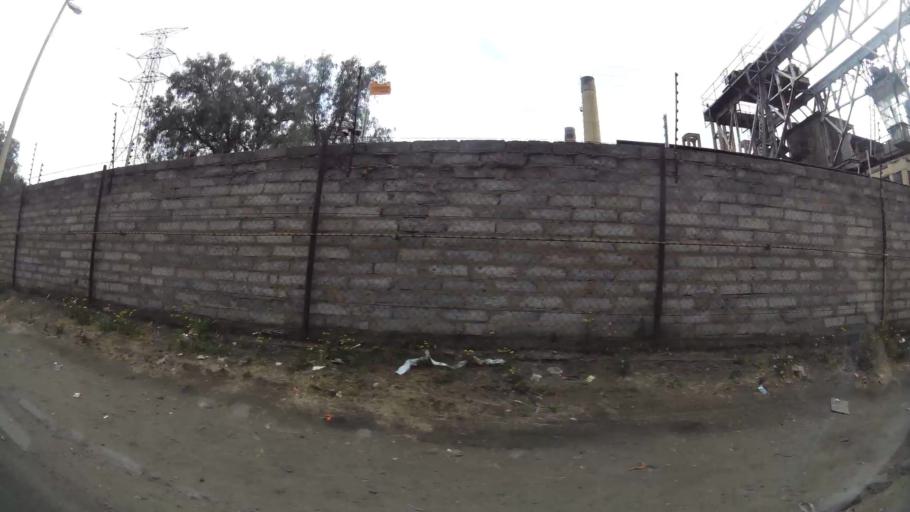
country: ZA
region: Orange Free State
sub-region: Mangaung Metropolitan Municipality
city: Bloemfontein
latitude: -29.1248
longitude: 26.2266
